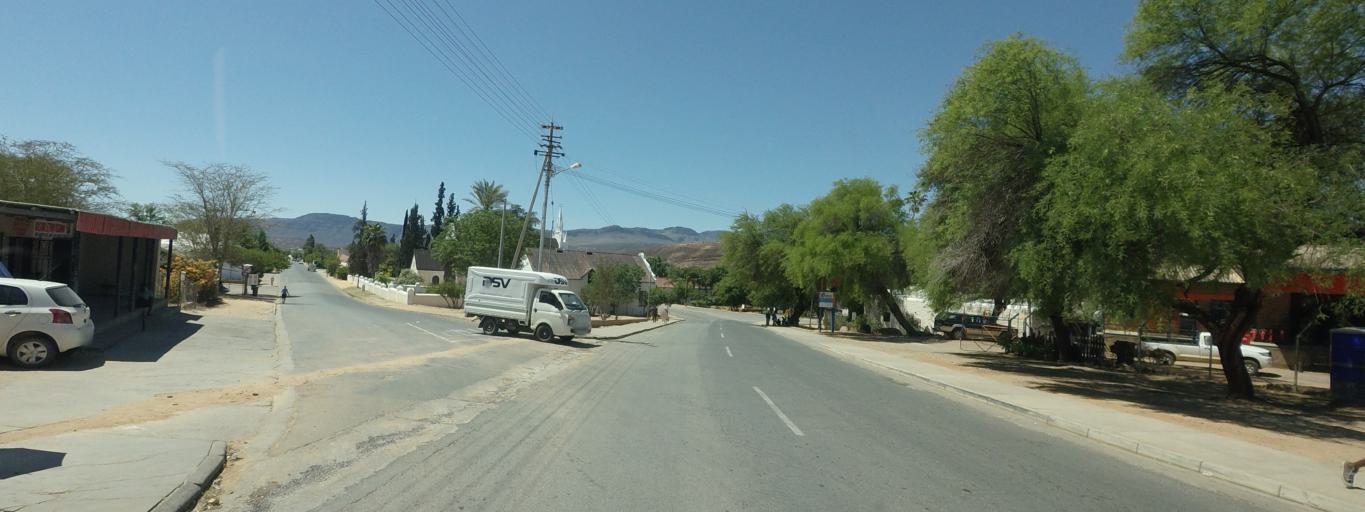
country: ZA
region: Western Cape
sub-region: West Coast District Municipality
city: Clanwilliam
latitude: -32.1816
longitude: 18.8933
